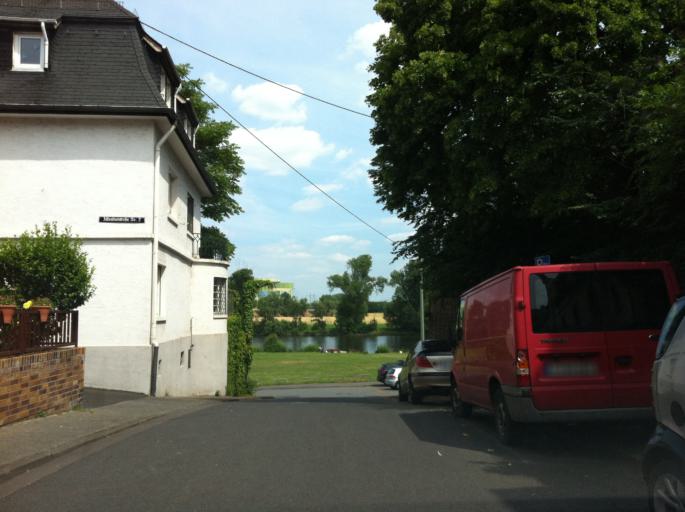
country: DE
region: Hesse
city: Kelsterbach
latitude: 50.0786
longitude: 8.5201
